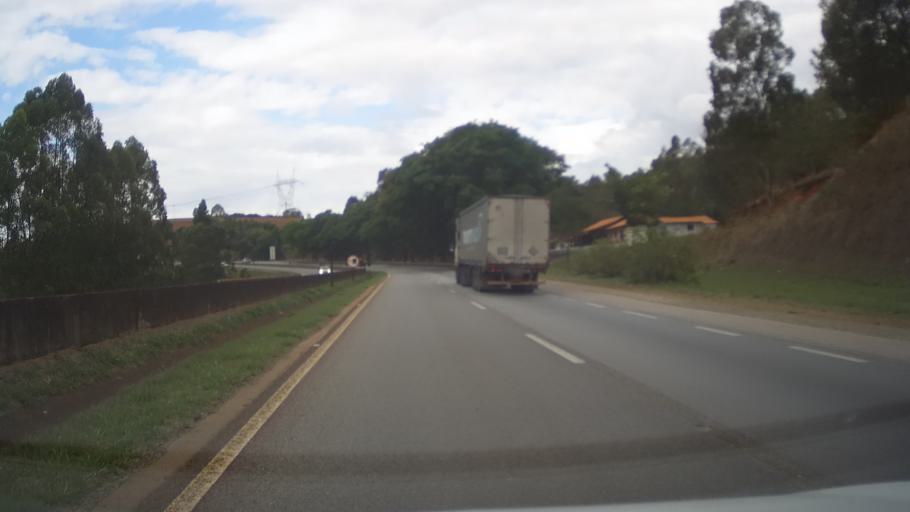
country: BR
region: Minas Gerais
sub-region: Igarape
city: Igarape
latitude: -20.2835
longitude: -44.4309
